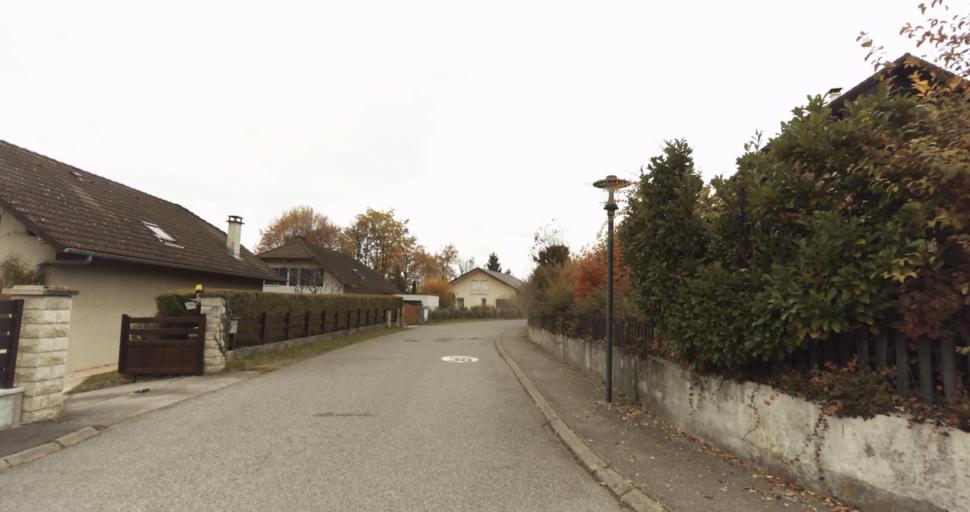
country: FR
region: Rhone-Alpes
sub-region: Departement de la Haute-Savoie
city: Pringy
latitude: 45.9460
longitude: 6.1270
